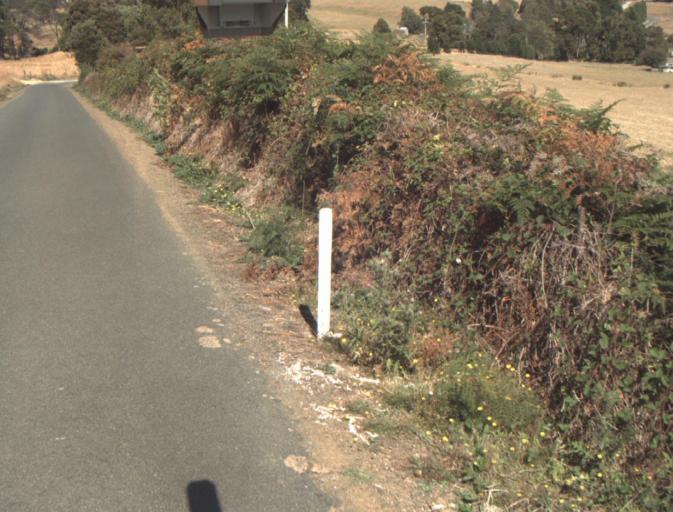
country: AU
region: Tasmania
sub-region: Launceston
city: Mayfield
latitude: -41.2310
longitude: 147.2444
